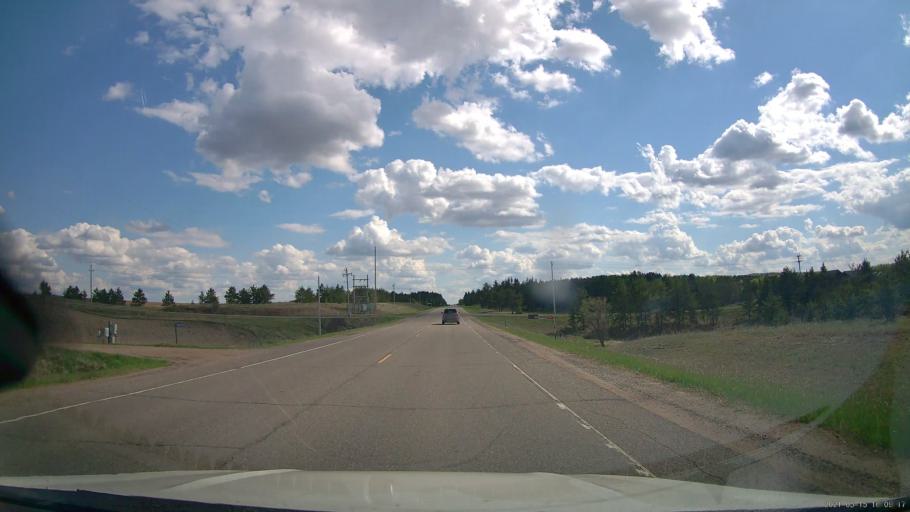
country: US
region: Minnesota
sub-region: Hubbard County
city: Park Rapids
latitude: 46.9514
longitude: -94.9528
